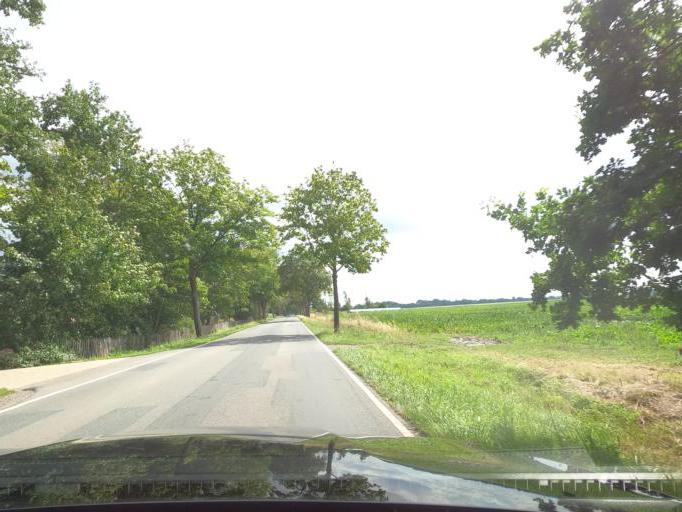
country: DE
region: Lower Saxony
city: Lehrte
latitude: 52.3577
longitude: 10.0189
